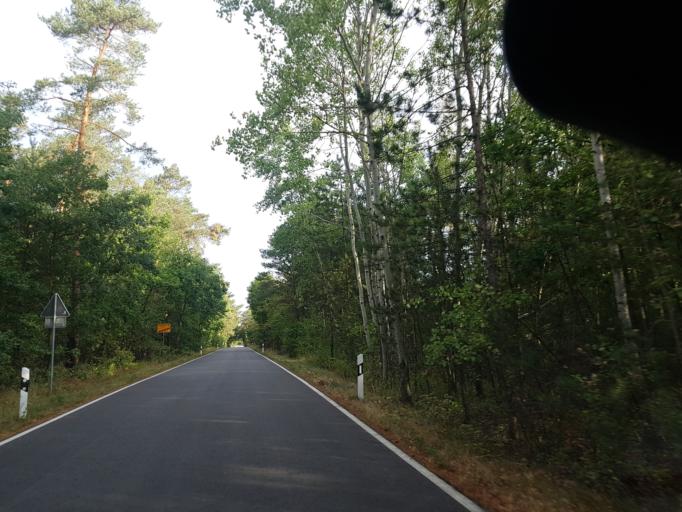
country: DE
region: Saxony-Anhalt
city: Holzdorf
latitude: 51.7875
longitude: 13.1109
